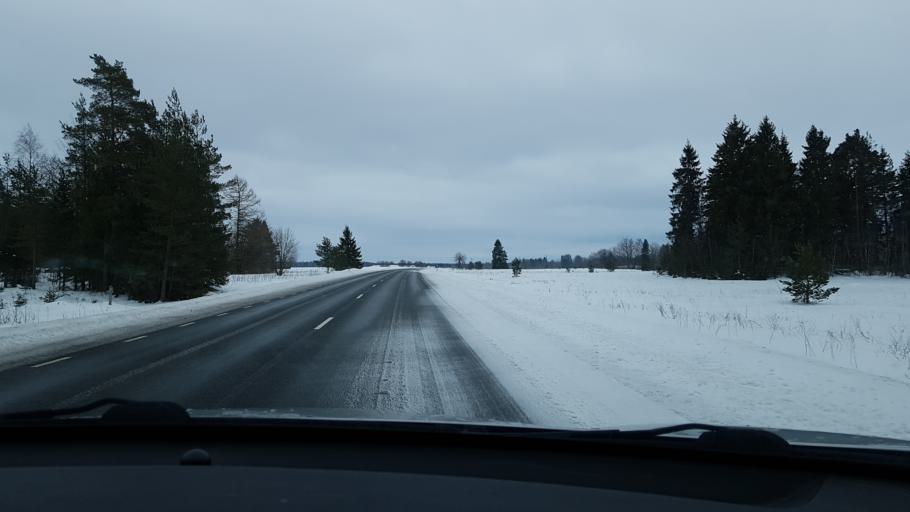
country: EE
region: Jaervamaa
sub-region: Jaerva-Jaani vald
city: Jarva-Jaani
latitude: 59.0915
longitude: 25.8300
